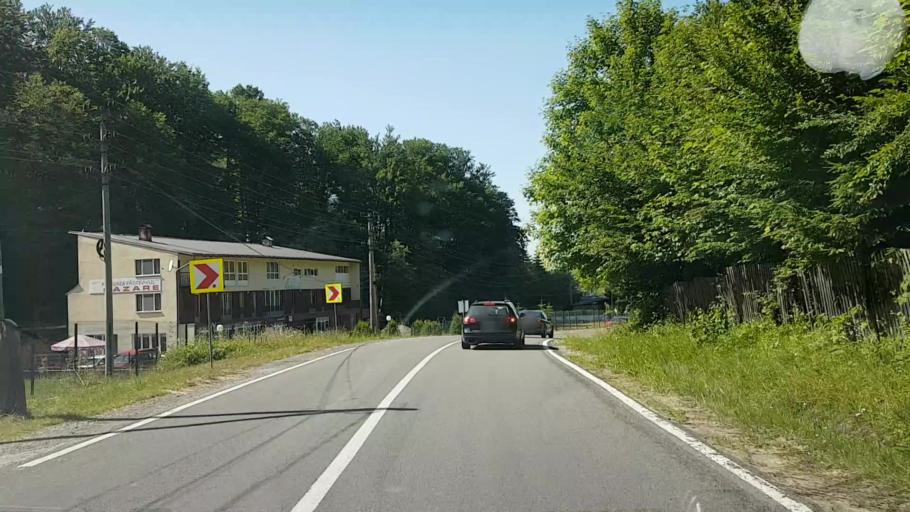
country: RO
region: Sibiu
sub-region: Comuna Cartisoara
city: Cartisoara
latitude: 45.6840
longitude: 24.5747
